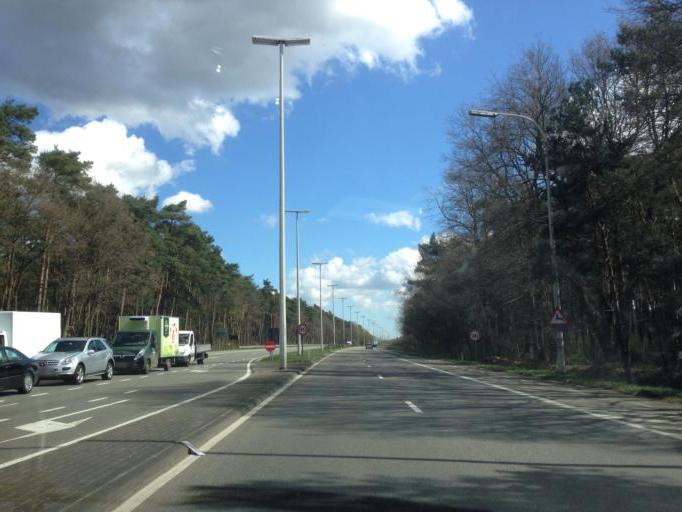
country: BE
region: Flanders
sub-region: Provincie Limburg
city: As
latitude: 50.9797
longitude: 5.5518
